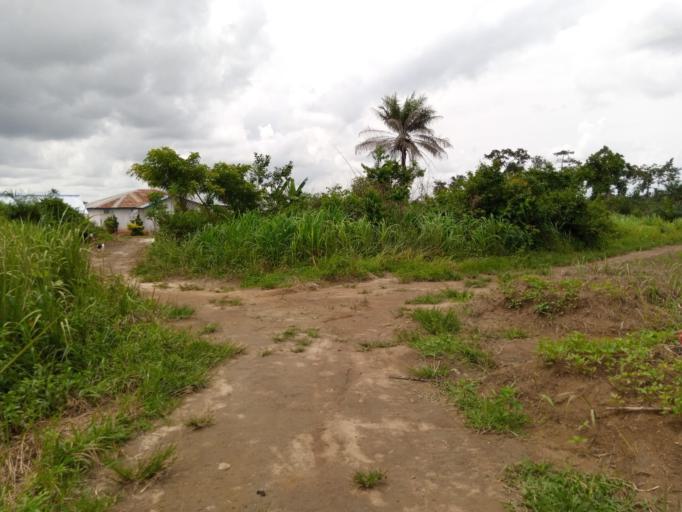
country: SL
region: Southern Province
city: Moyamba
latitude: 8.1693
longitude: -12.4144
